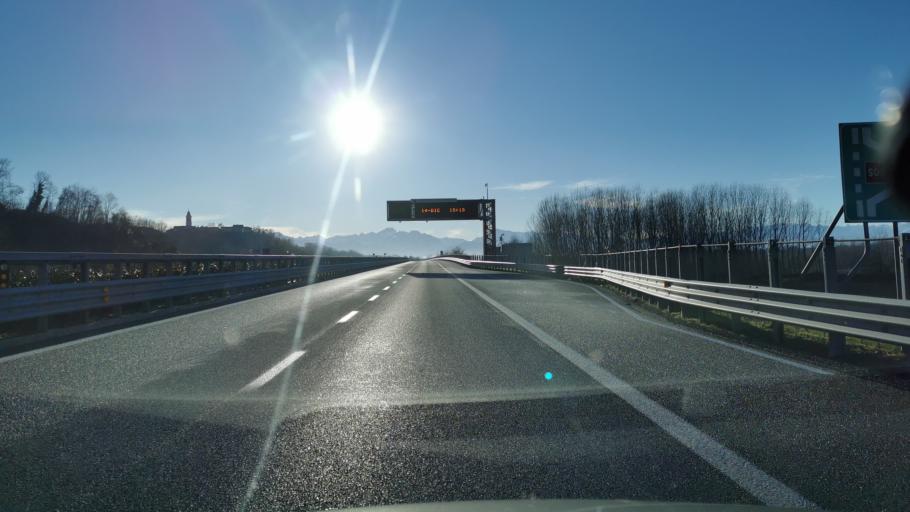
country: IT
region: Piedmont
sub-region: Provincia di Cuneo
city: Montanera
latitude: 44.4711
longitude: 7.6707
